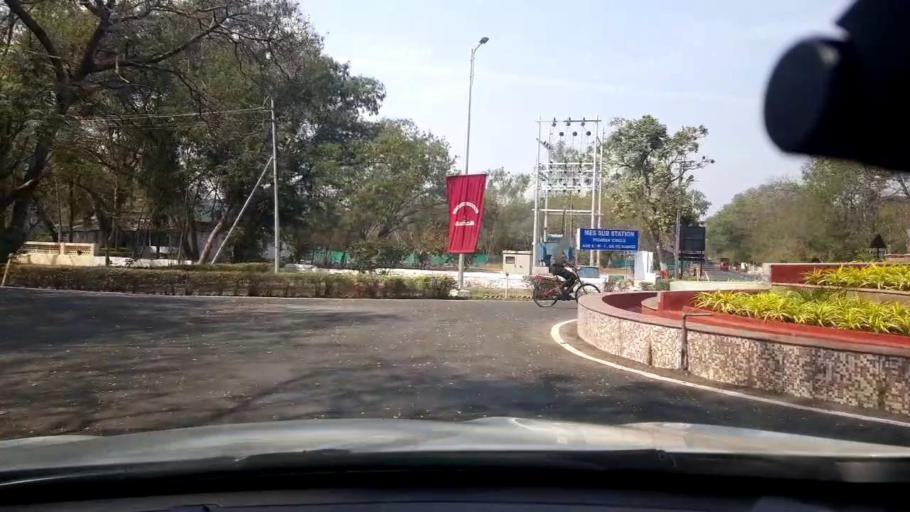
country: IN
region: Maharashtra
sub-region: Pune Division
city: Shivaji Nagar
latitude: 18.5454
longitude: 73.8639
